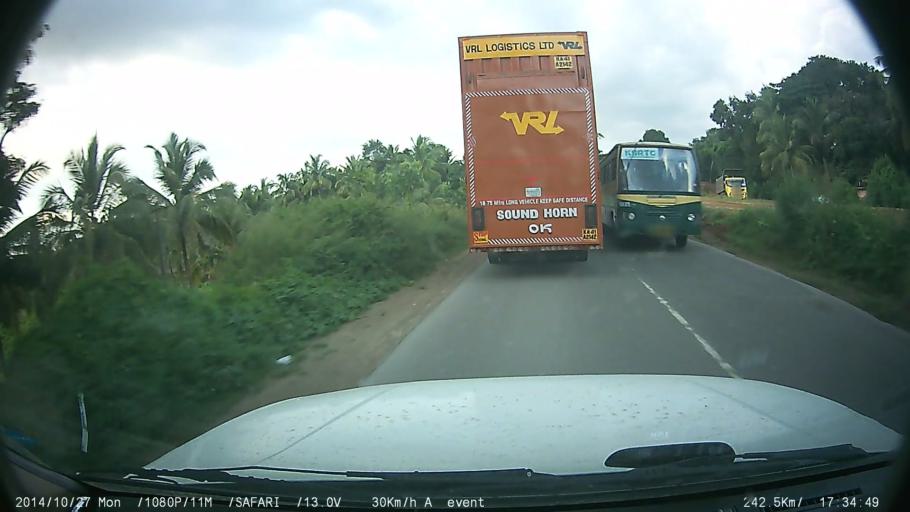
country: IN
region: Kerala
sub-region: Palakkad district
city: Palakkad
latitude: 10.6844
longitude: 76.5794
